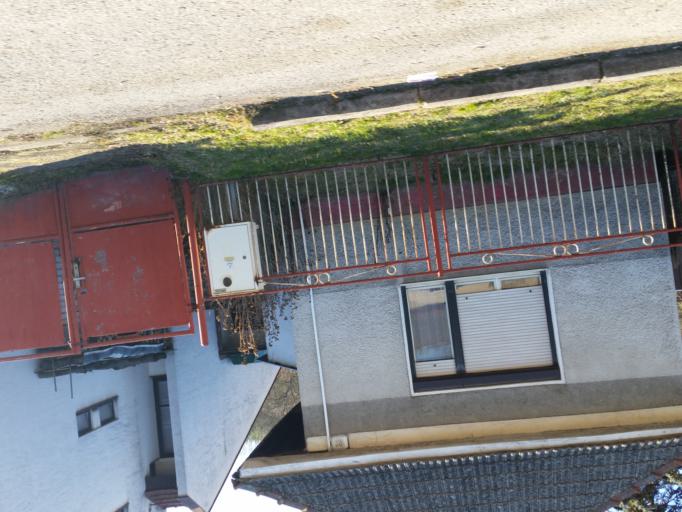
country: SK
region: Trnavsky
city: Vrbove
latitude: 48.6584
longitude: 17.7189
